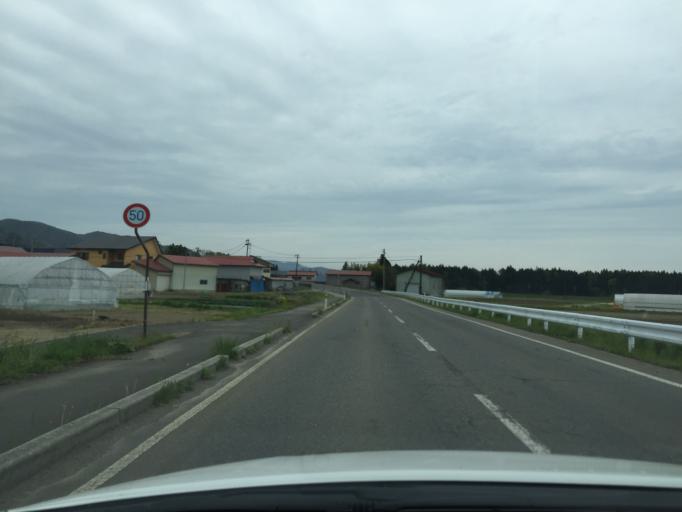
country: JP
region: Fukushima
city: Inawashiro
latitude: 37.5453
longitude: 140.1266
